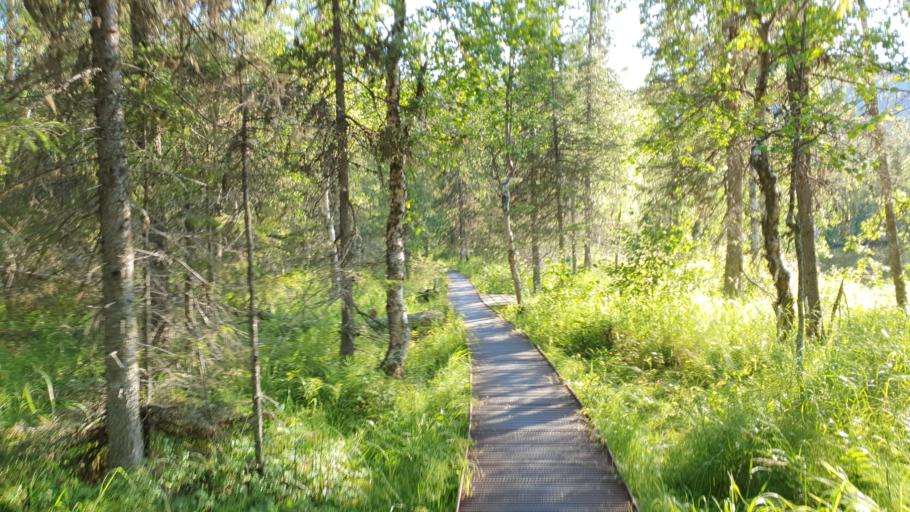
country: FI
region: Lapland
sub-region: Tunturi-Lappi
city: Kolari
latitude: 67.5975
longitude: 24.2549
